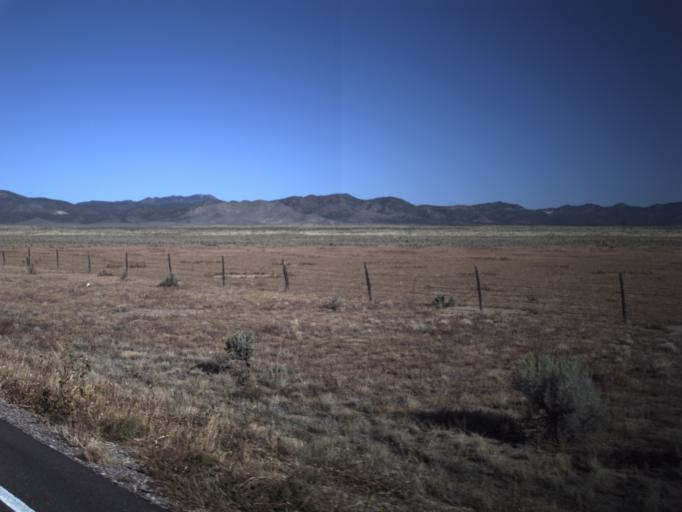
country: US
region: Utah
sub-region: Washington County
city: Enterprise
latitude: 37.7804
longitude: -113.8582
